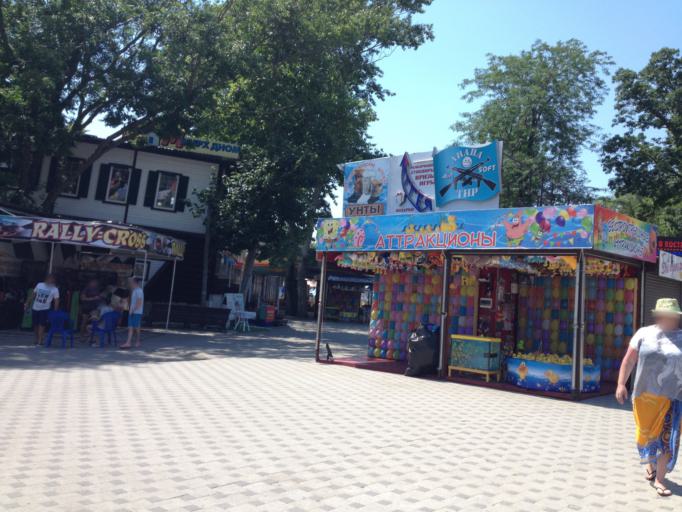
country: RU
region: Krasnodarskiy
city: Anapa
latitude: 44.8963
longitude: 37.3147
